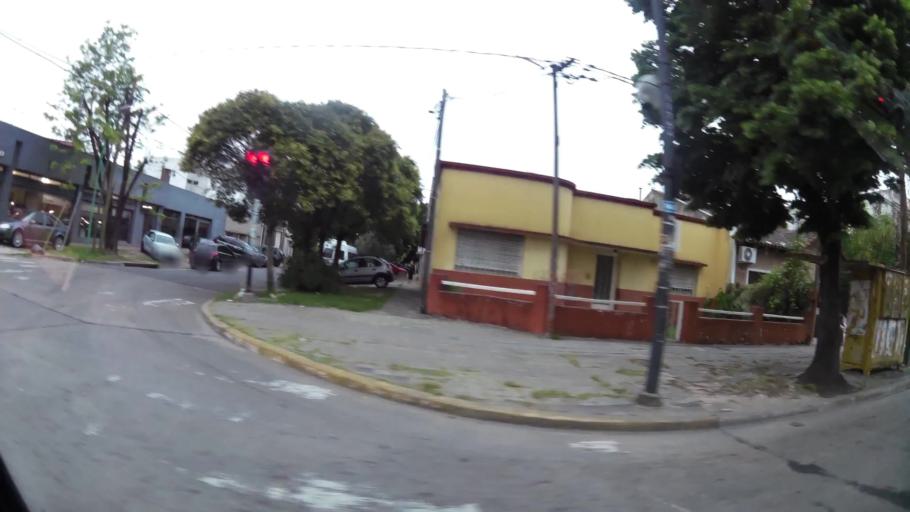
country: AR
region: Buenos Aires
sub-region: Partido de La Plata
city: La Plata
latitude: -34.8989
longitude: -57.9713
